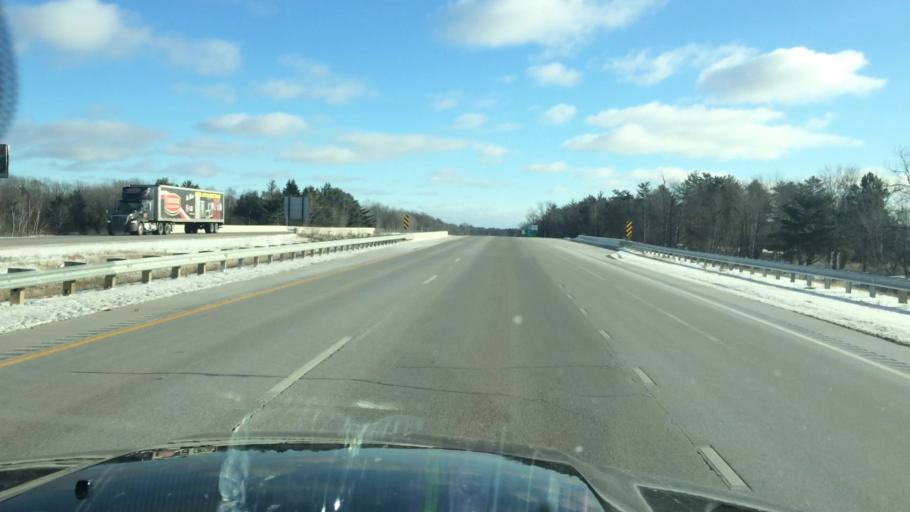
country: US
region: Wisconsin
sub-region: Portage County
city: Stevens Point
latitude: 44.5482
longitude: -89.5713
